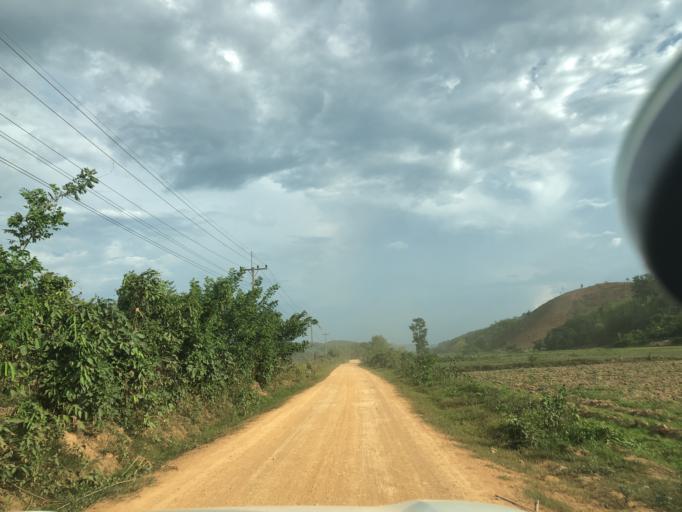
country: TH
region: Loei
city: Chiang Khan
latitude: 18.0100
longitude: 101.4204
